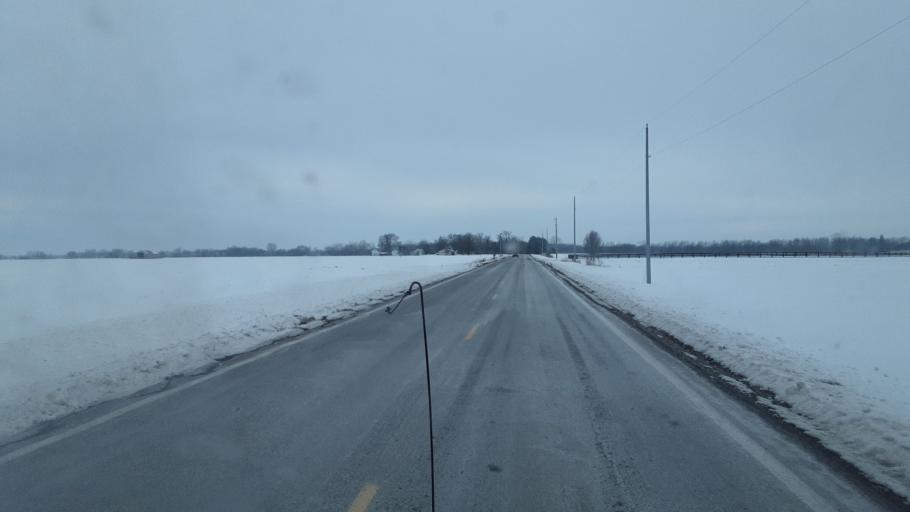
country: US
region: Ohio
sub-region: Champaign County
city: Mechanicsburg
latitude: 40.1204
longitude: -83.4437
